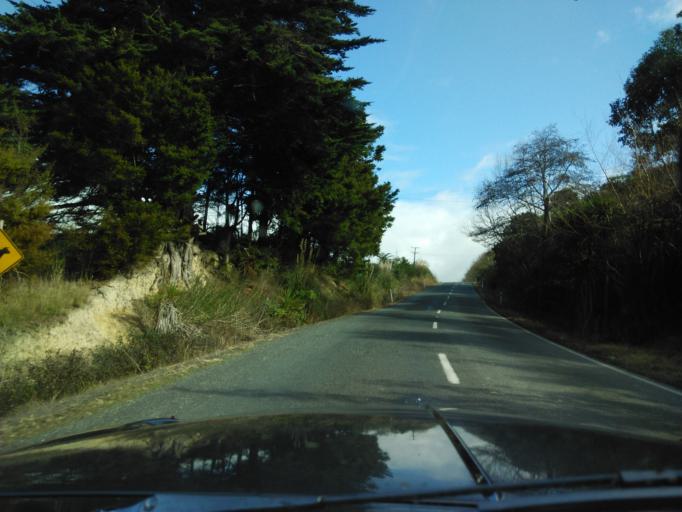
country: NZ
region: Auckland
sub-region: Auckland
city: Wellsford
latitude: -36.1641
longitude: 174.4322
